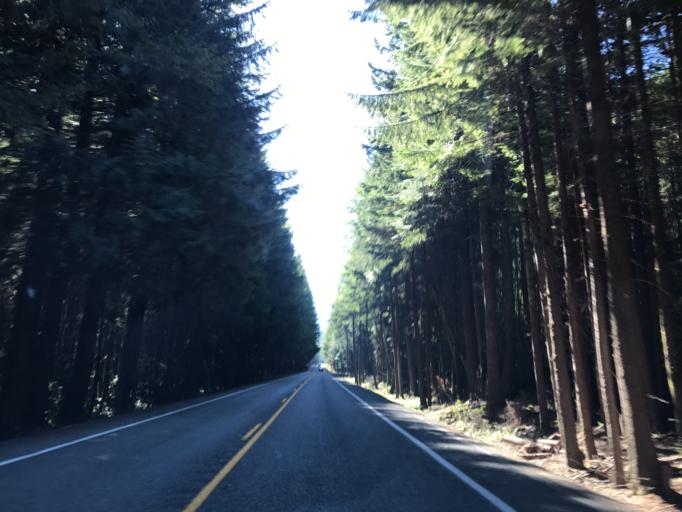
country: US
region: Washington
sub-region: King County
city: Riverbend
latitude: 47.1143
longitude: -121.6042
